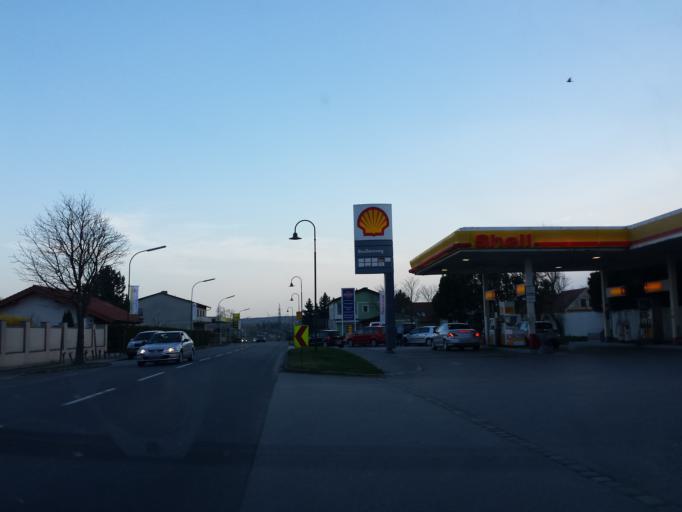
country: AT
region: Lower Austria
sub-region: Politischer Bezirk Mistelbach
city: Poysdorf
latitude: 48.6608
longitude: 16.6288
